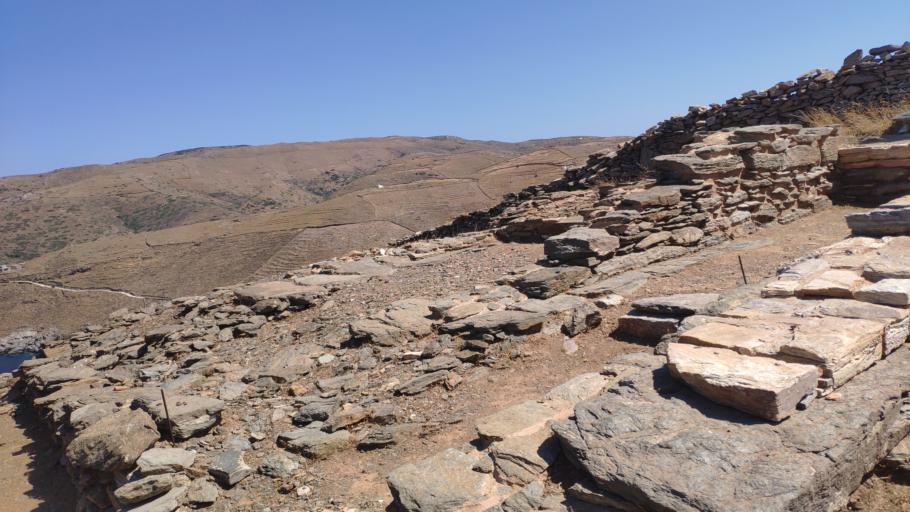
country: GR
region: South Aegean
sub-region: Nomos Kykladon
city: Kythnos
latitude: 37.4085
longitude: 24.3949
